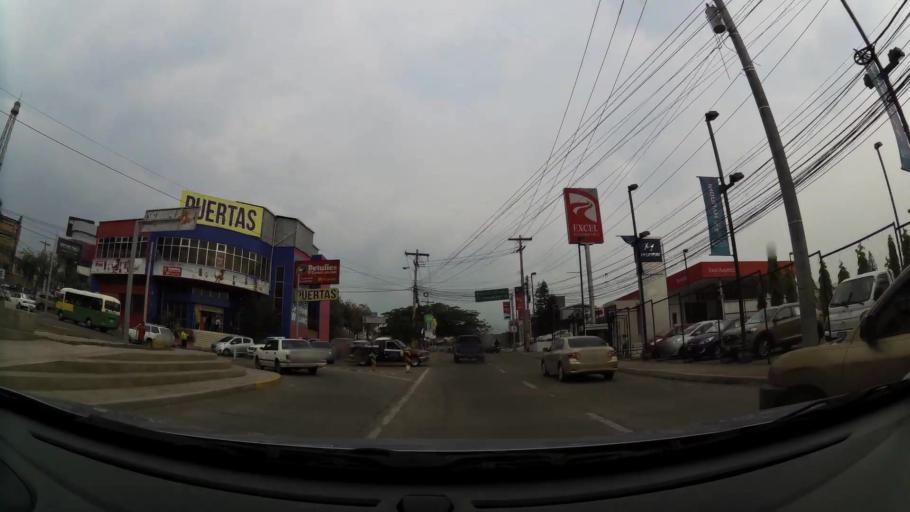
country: HN
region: Francisco Morazan
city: Tegucigalpa
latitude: 14.0876
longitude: -87.1987
